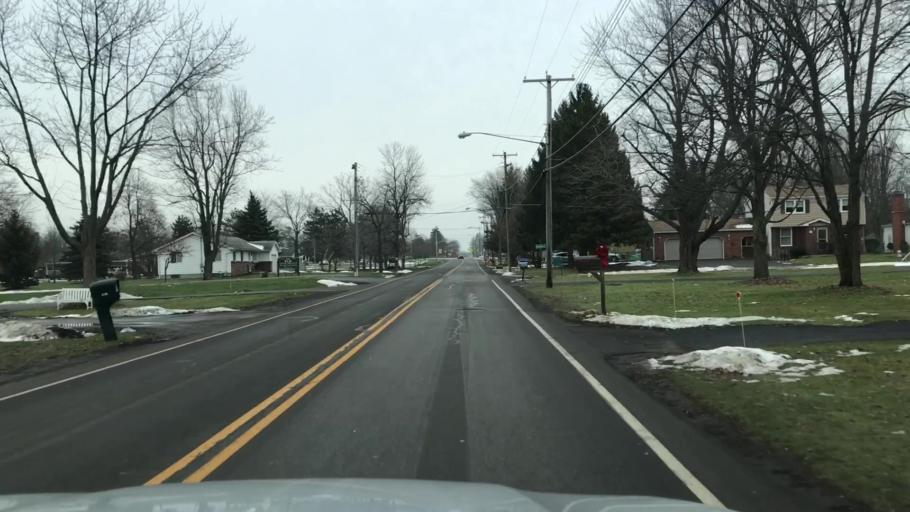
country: US
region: New York
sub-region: Erie County
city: Hamburg
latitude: 42.7514
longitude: -78.8287
